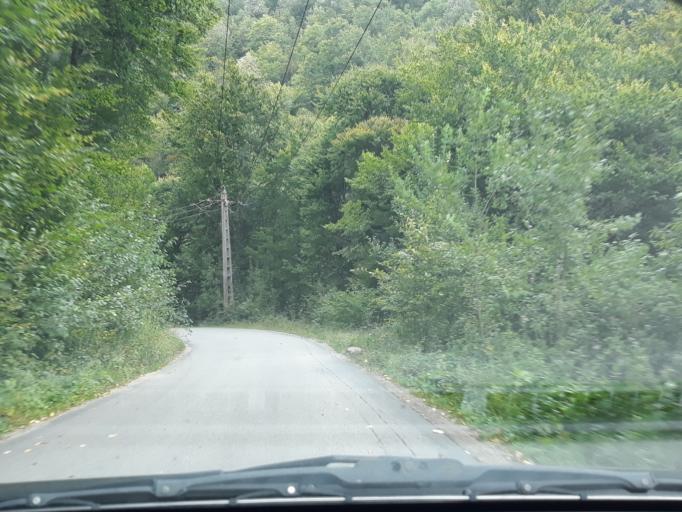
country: RO
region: Bihor
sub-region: Comuna Pietroasa
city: Pietroasa
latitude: 46.5879
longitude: 22.6231
